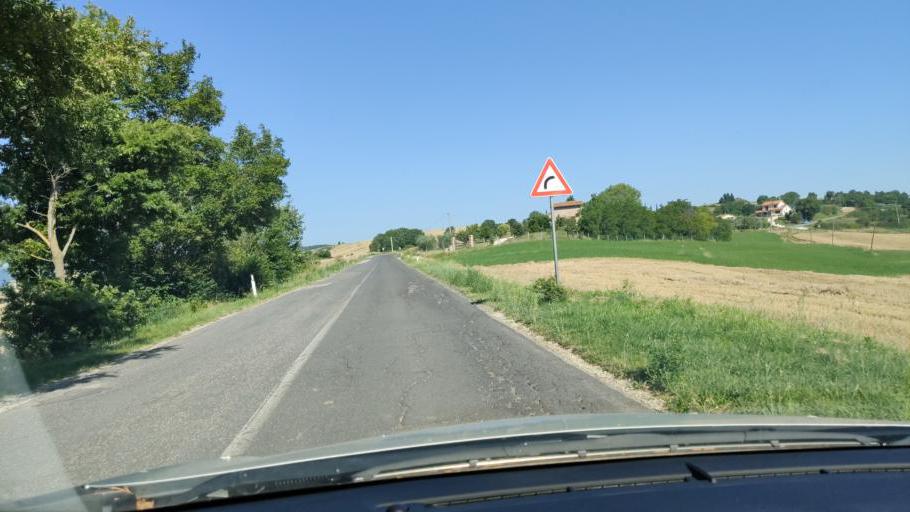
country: IT
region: Umbria
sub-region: Provincia di Terni
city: Avigliano Umbro
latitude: 42.6724
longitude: 12.4427
